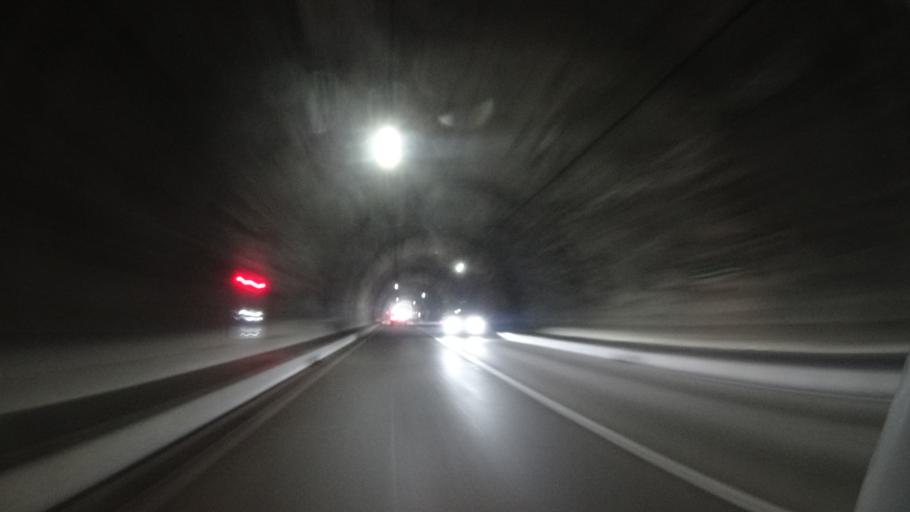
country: JP
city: Asahi
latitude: 35.9736
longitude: 135.9642
